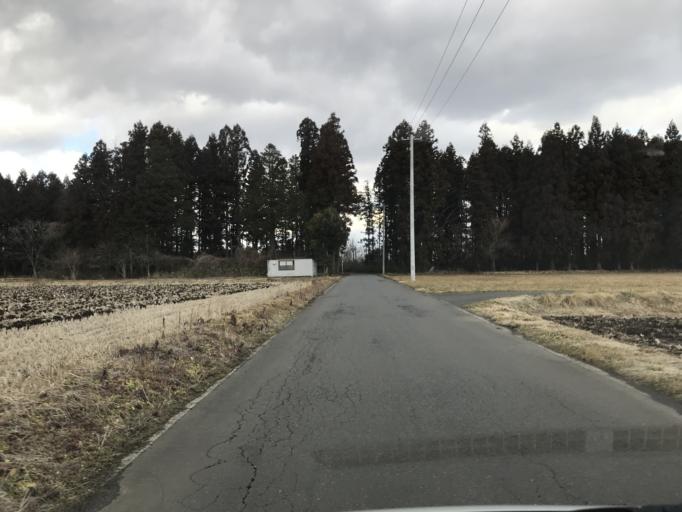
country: JP
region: Iwate
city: Mizusawa
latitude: 39.0834
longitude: 141.1116
